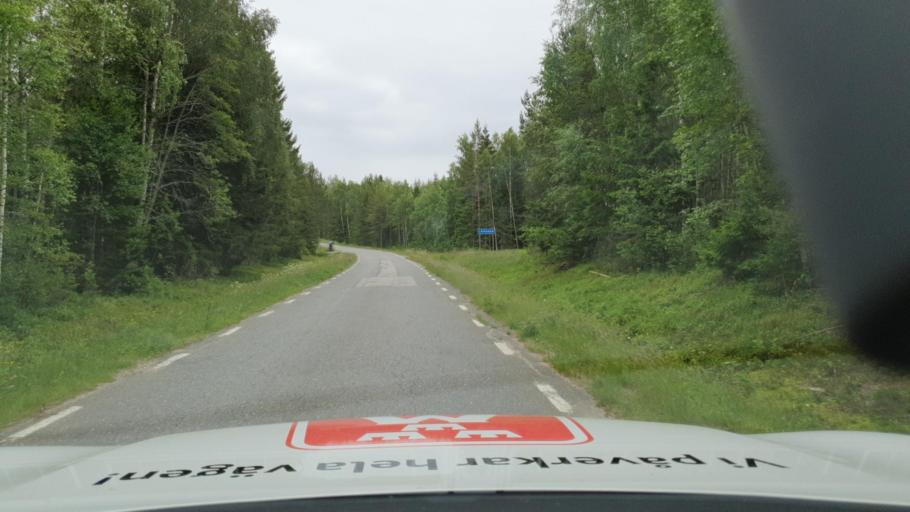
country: SE
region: Vaesterbotten
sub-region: Nordmalings Kommun
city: Nordmaling
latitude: 63.4273
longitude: 19.4945
